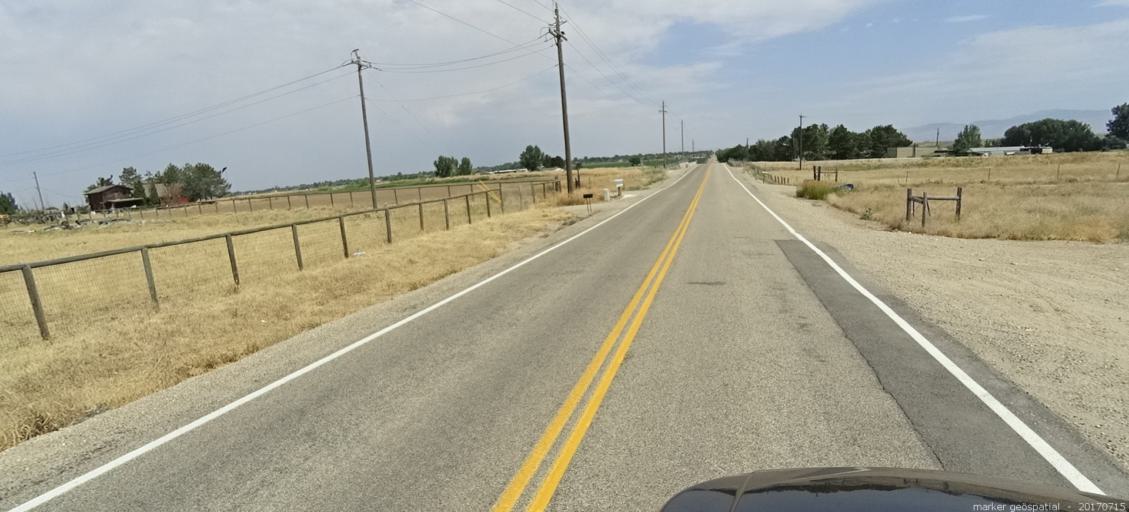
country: US
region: Idaho
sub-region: Ada County
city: Garden City
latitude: 43.5279
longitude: -116.2742
